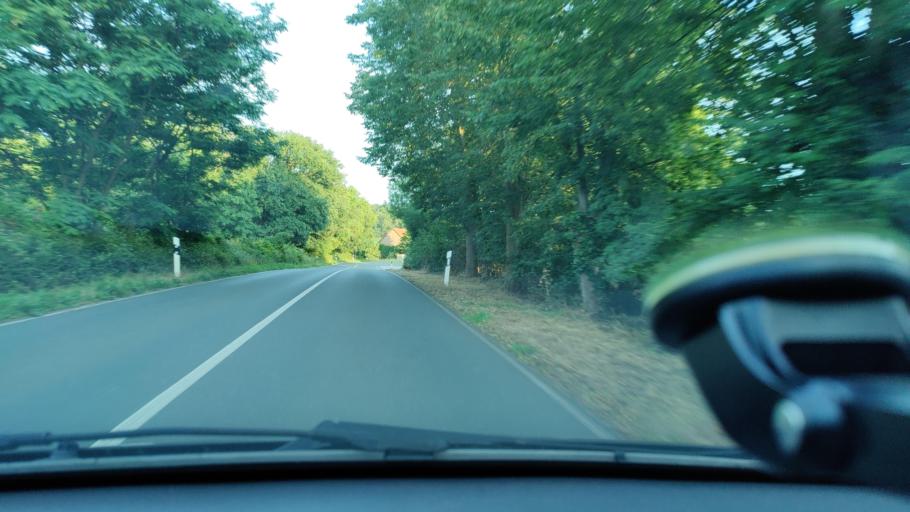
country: DE
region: North Rhine-Westphalia
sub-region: Regierungsbezirk Dusseldorf
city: Kamp-Lintfort
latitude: 51.4787
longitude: 6.5217
